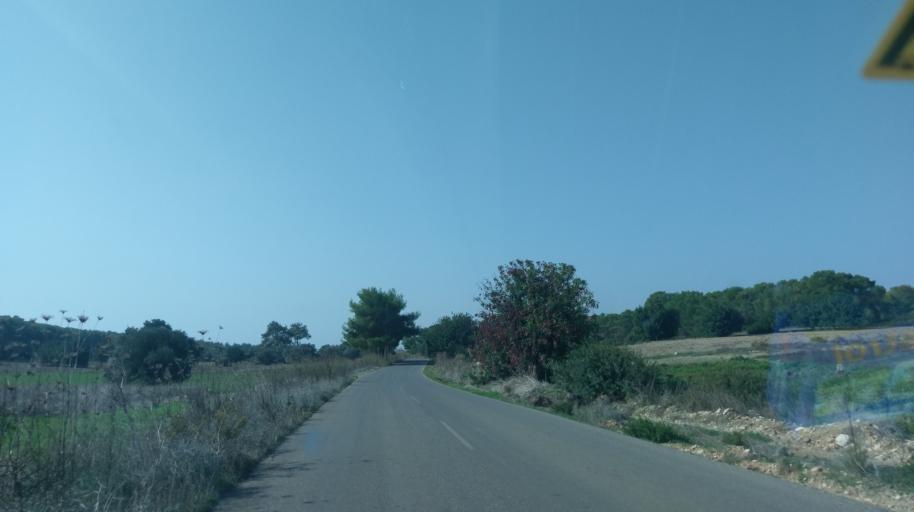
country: CY
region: Lefkosia
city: Morfou
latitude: 35.3035
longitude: 33.0207
